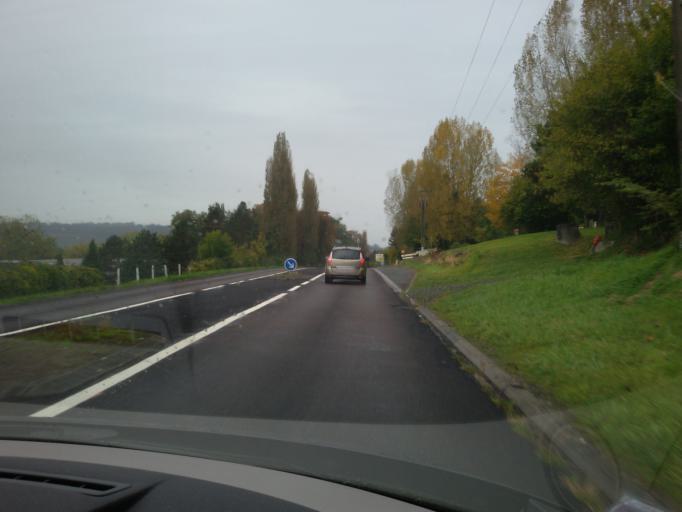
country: FR
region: Lower Normandy
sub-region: Departement du Calvados
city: Houlgate
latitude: 49.2978
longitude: -0.0589
